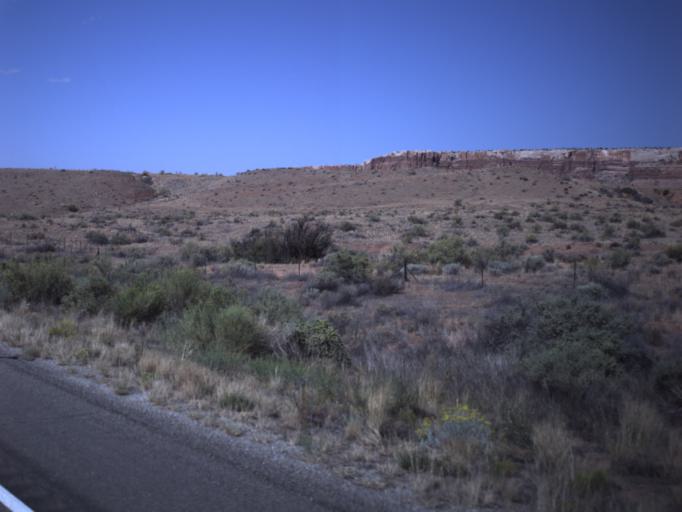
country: US
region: Utah
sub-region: San Juan County
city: Blanding
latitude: 37.2763
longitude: -109.5856
